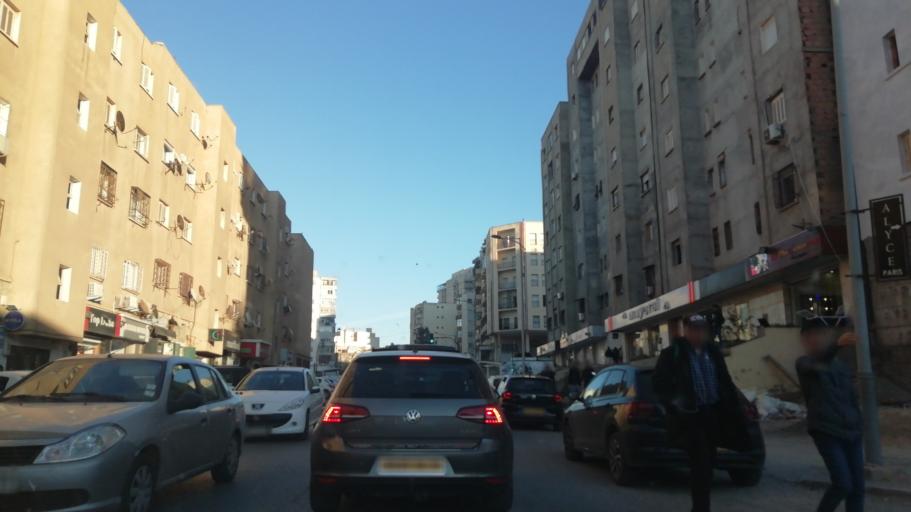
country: DZ
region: Oran
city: Bir el Djir
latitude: 35.7229
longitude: -0.5887
